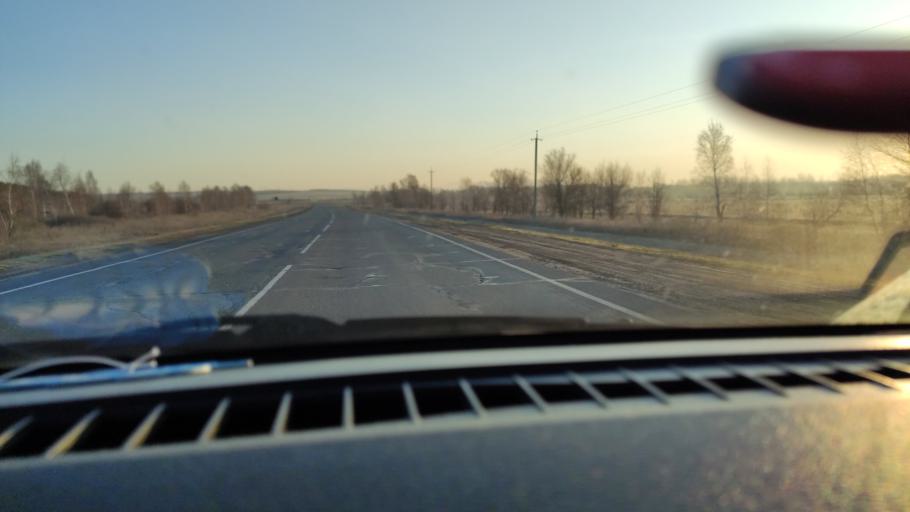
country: RU
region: Saratov
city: Sinodskoye
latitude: 52.0355
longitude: 46.7284
